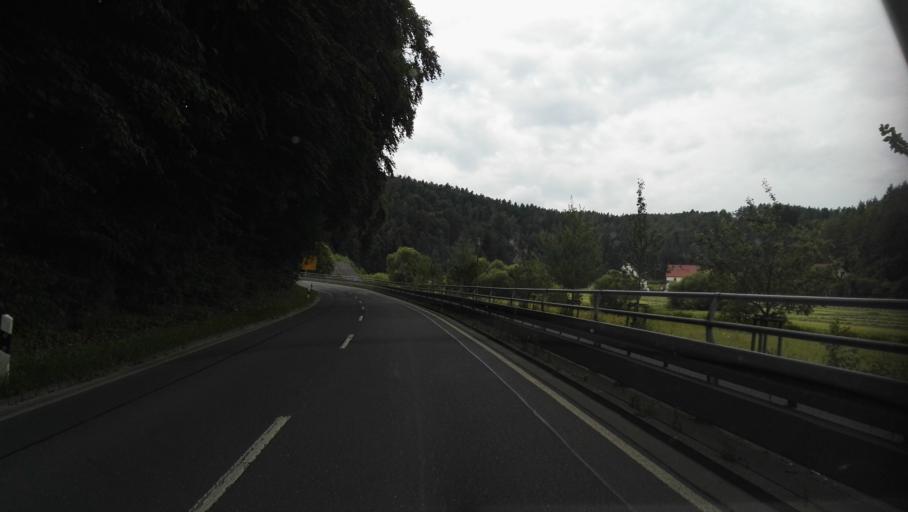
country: DE
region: Bavaria
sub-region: Upper Franconia
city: Waischenfeld
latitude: 49.8512
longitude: 11.3393
